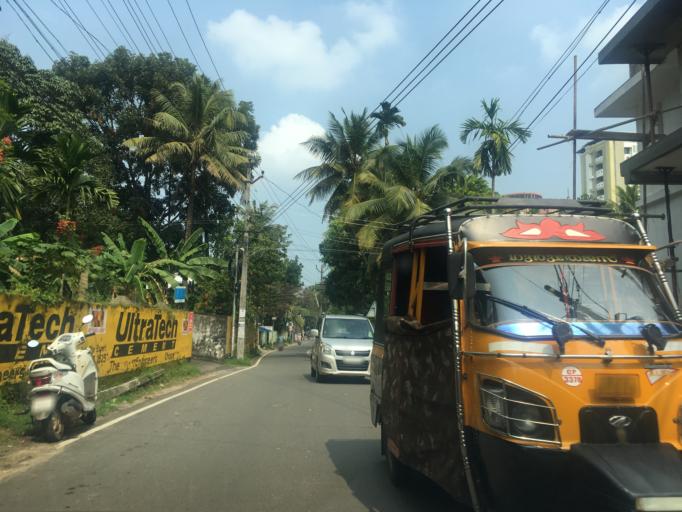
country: IN
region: Kerala
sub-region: Ernakulam
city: Elur
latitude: 10.0389
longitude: 76.3064
